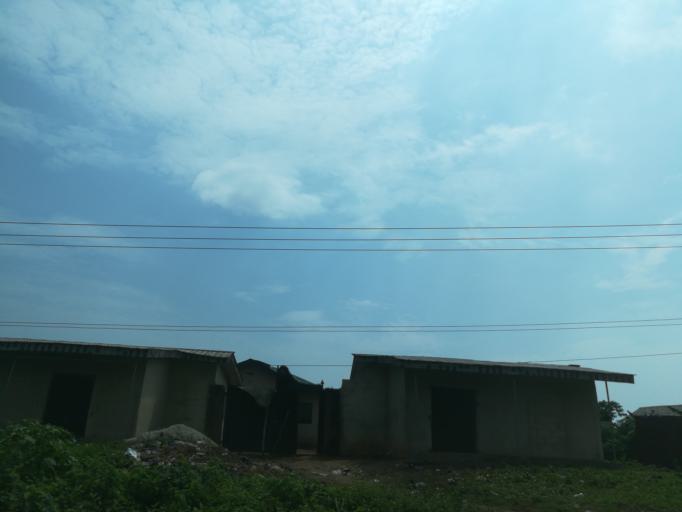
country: NG
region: Lagos
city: Ikorodu
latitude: 6.5986
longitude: 3.6298
